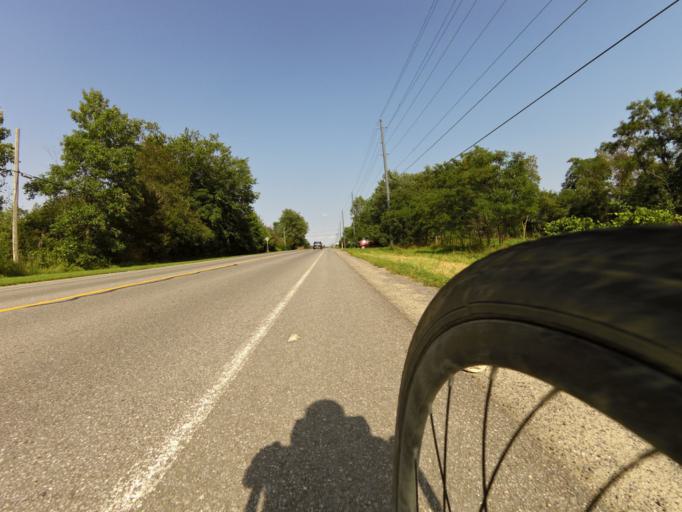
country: CA
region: Ontario
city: Kingston
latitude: 44.3016
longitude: -76.6959
